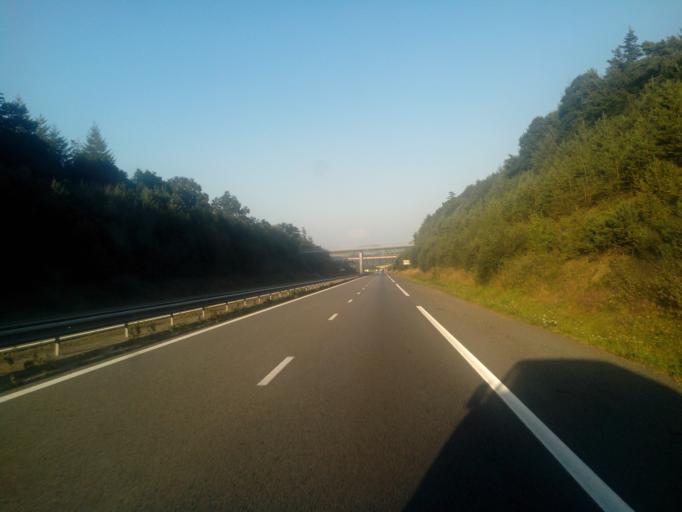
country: FR
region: Brittany
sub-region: Departement du Morbihan
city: Saint-Gonnery
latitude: 48.1298
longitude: -2.8215
